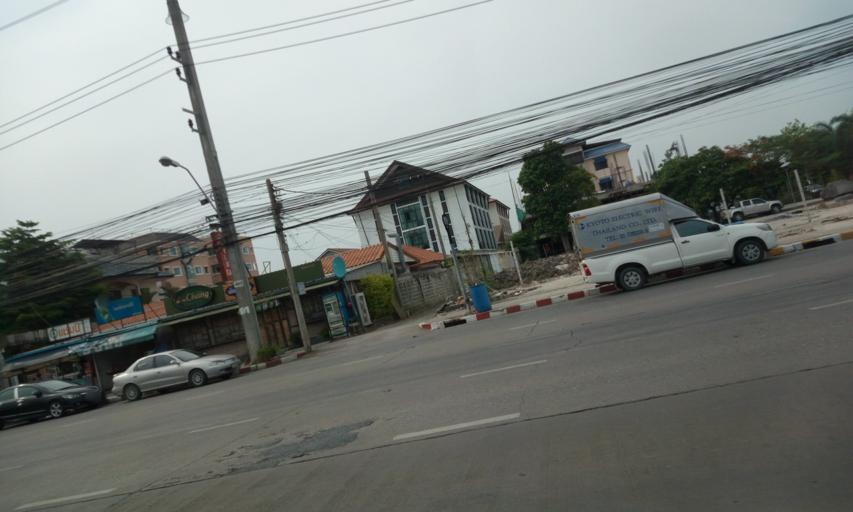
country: TH
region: Bangkok
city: Lat Krabang
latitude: 13.7218
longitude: 100.7722
